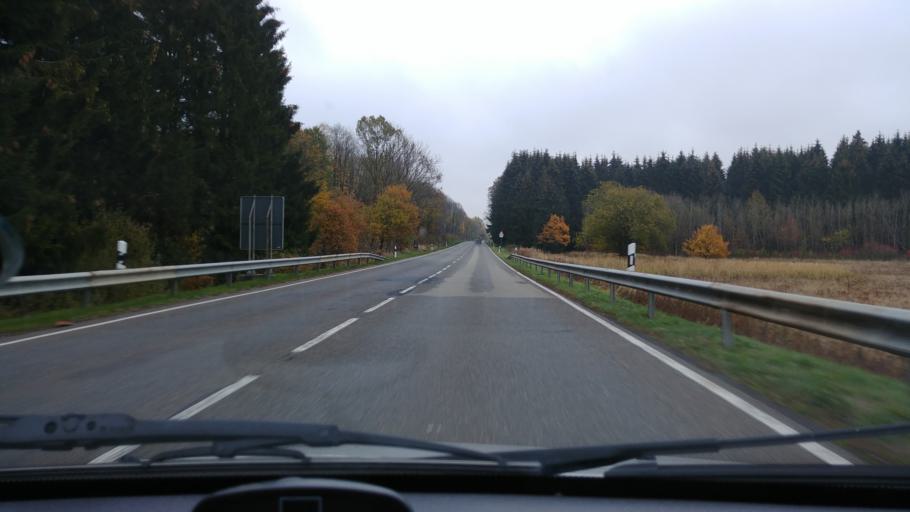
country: DE
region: Rheinland-Pfalz
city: Langenhahn
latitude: 50.5800
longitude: 7.9308
